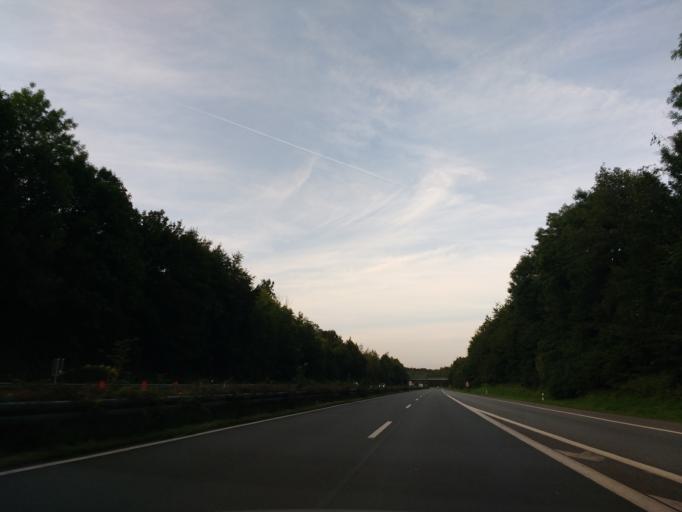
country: DE
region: North Rhine-Westphalia
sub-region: Regierungsbezirk Detmold
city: Wunnenberg
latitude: 51.5854
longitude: 8.7225
